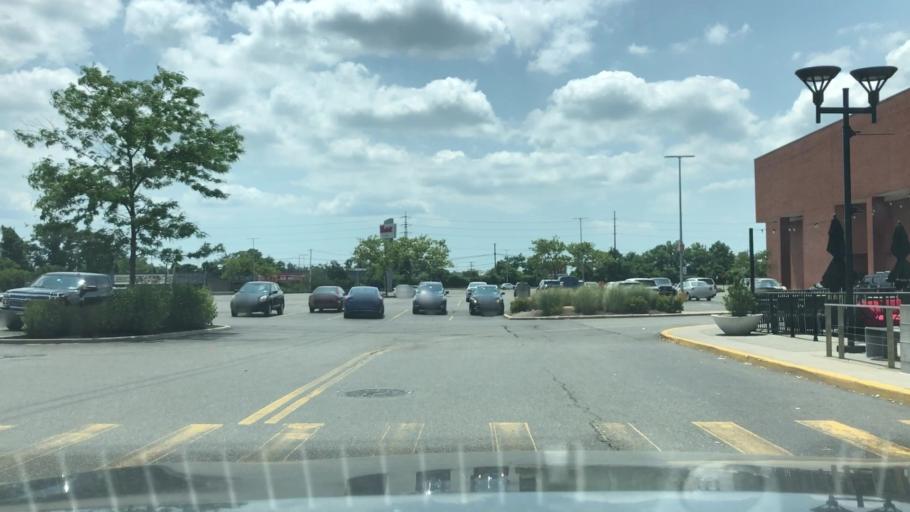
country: US
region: New York
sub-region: Nassau County
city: East Massapequa
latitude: 40.6815
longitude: -73.4339
